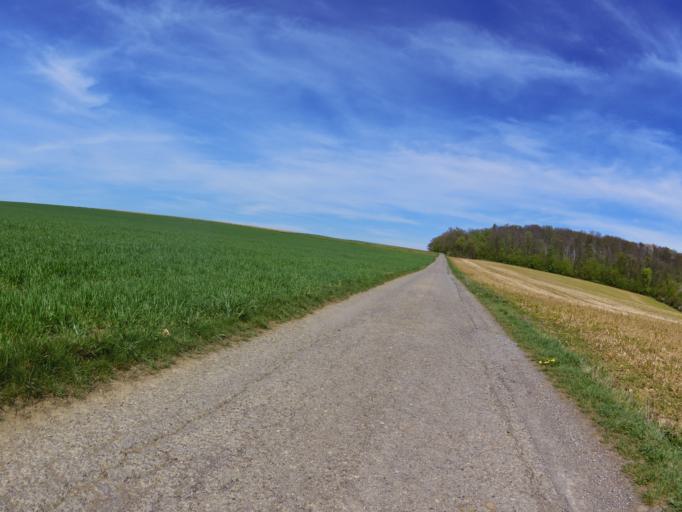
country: DE
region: Bavaria
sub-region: Regierungsbezirk Unterfranken
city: Rimpar
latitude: 49.8552
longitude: 9.9779
